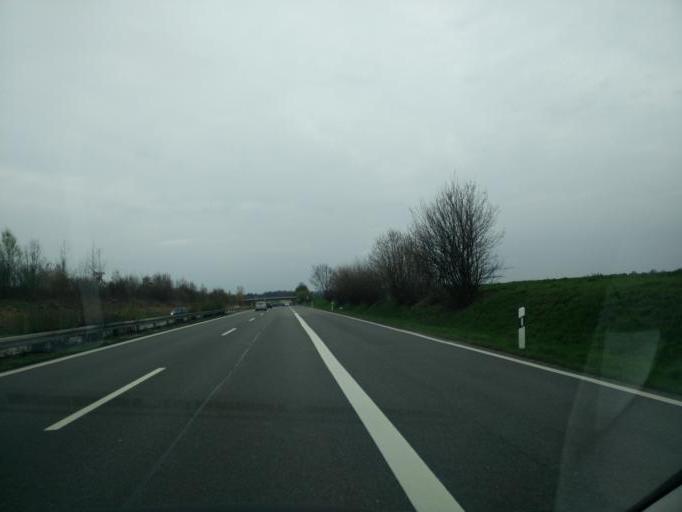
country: DE
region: Baden-Wuerttemberg
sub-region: Tuebingen Region
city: Pliezhausen
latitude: 48.5811
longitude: 9.1733
